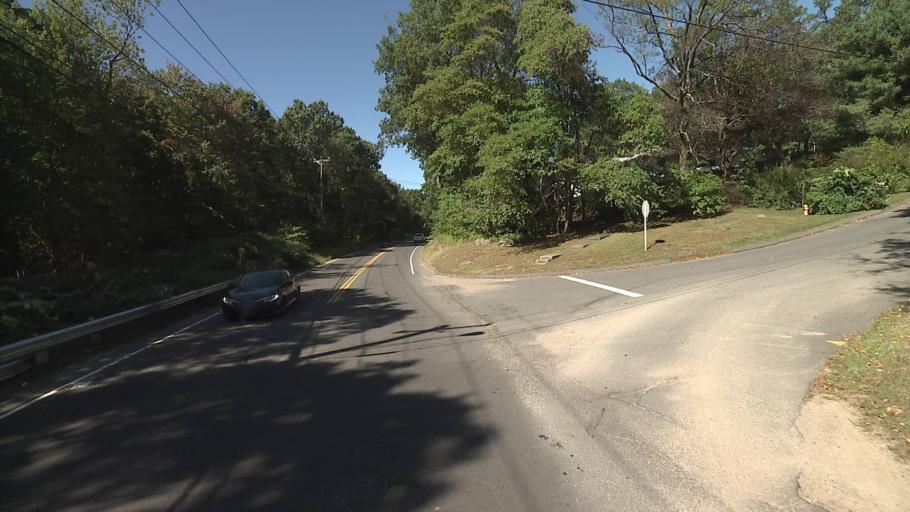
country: US
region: Connecticut
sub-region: New Haven County
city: Prospect
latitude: 41.5261
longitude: -73.0004
